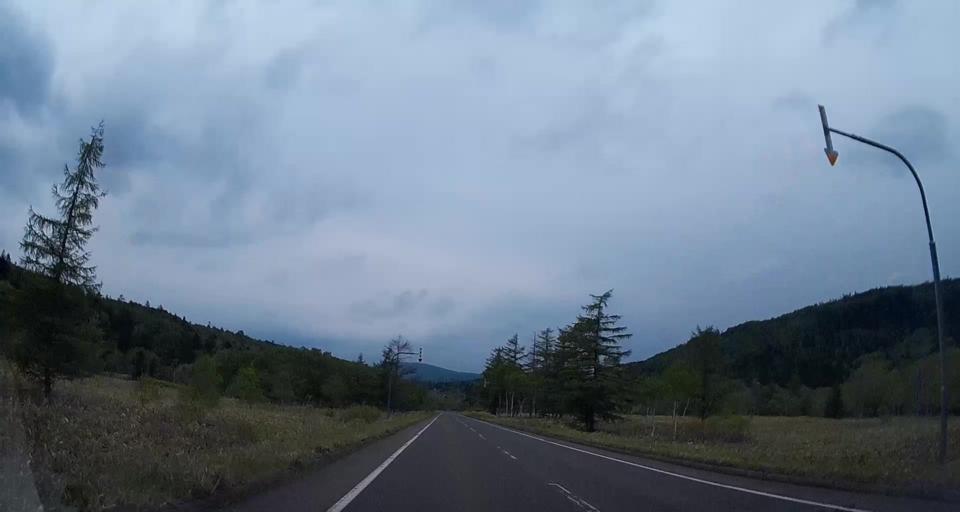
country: JP
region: Hokkaido
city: Shiraoi
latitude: 42.6763
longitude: 141.1475
